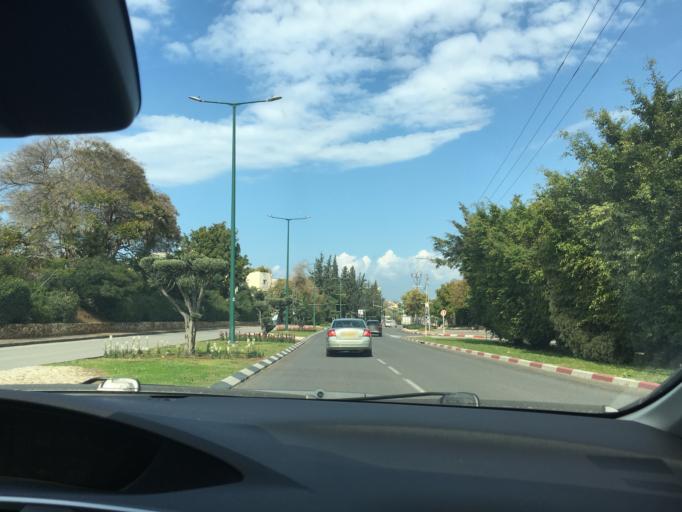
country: IL
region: Central District
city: Ra'anana
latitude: 32.1715
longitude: 34.8524
